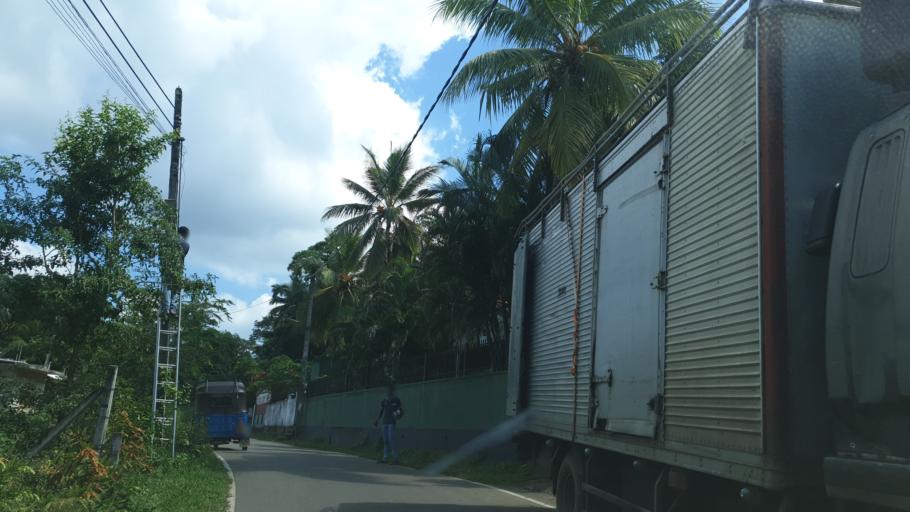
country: LK
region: Western
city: Panadura
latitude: 6.6830
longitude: 79.9429
